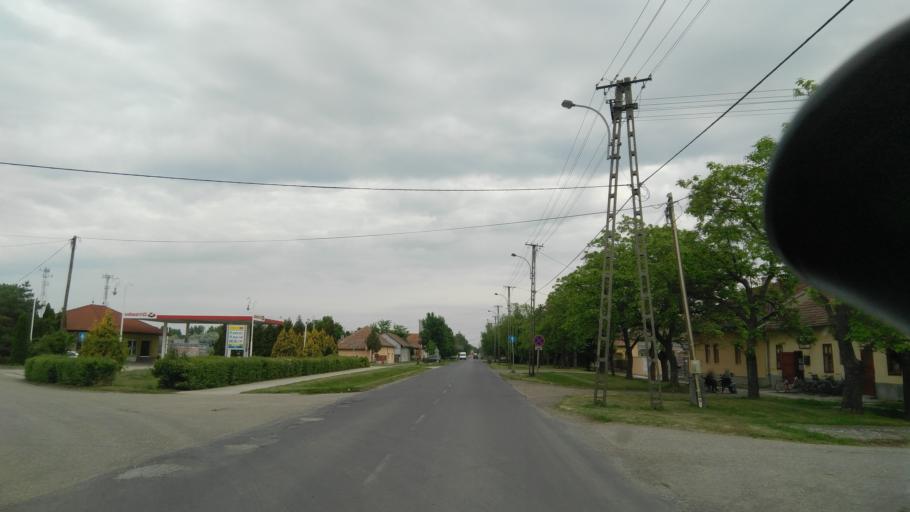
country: HU
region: Bekes
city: Veszto
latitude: 46.9138
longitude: 21.2582
